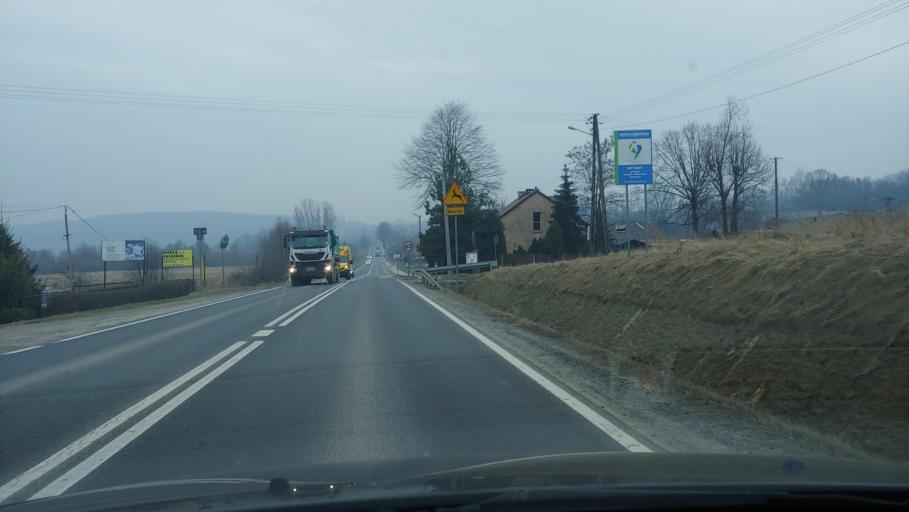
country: PL
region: Lesser Poland Voivodeship
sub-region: Powiat krakowski
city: Rudawa
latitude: 50.1206
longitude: 19.6903
